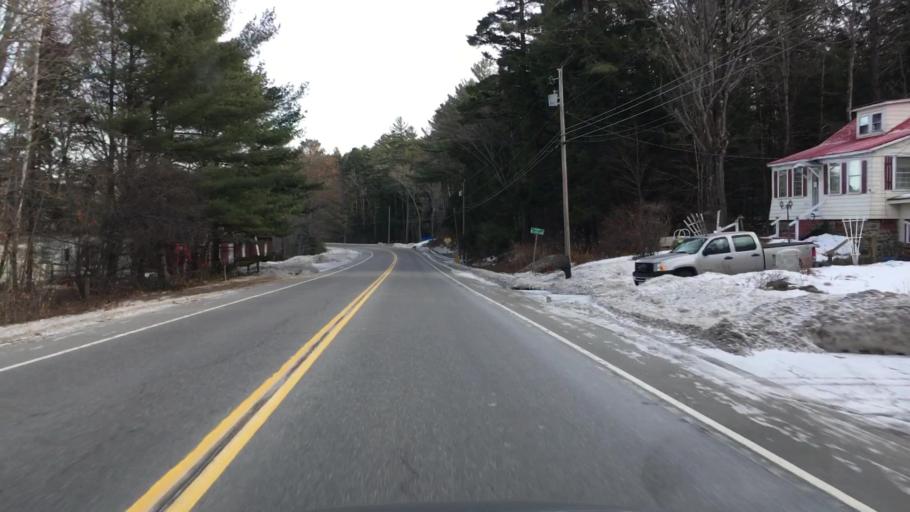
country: US
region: New Hampshire
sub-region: Sullivan County
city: Sunapee
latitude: 43.3421
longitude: -72.0822
